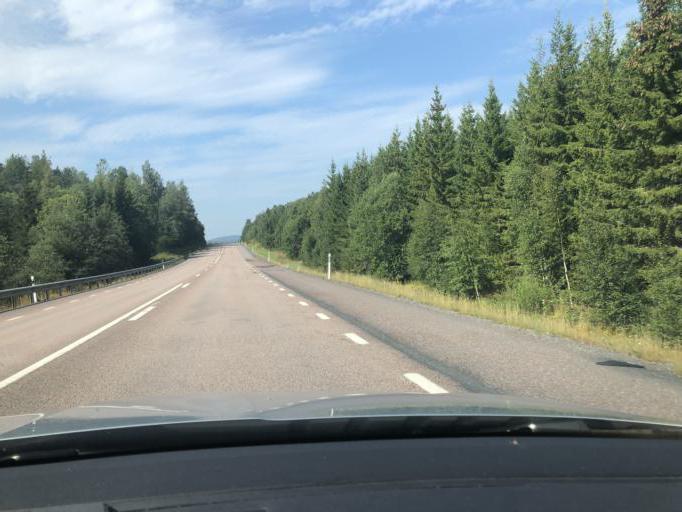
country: SE
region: Vaesternorrland
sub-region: Haernoesands Kommun
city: Haernoesand
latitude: 62.7937
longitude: 17.8980
